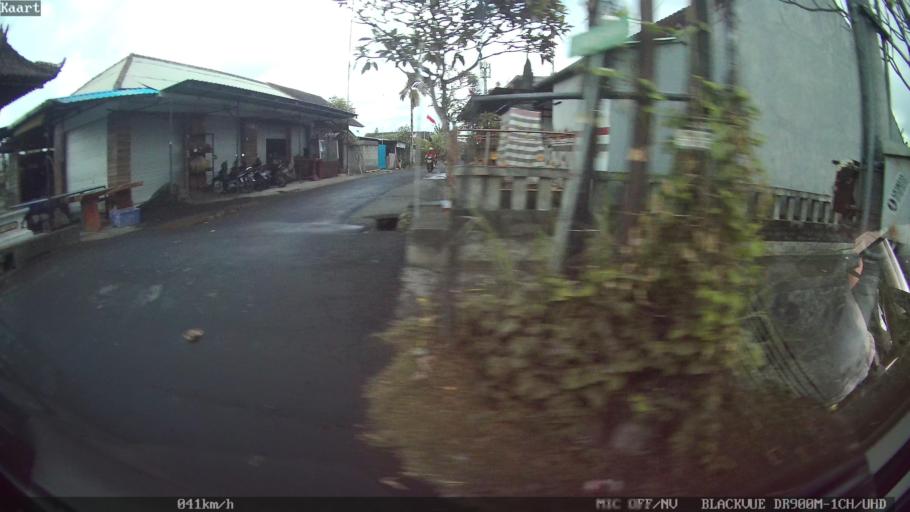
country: ID
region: Bali
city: Banjar Batur
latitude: -8.6020
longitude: 115.2061
